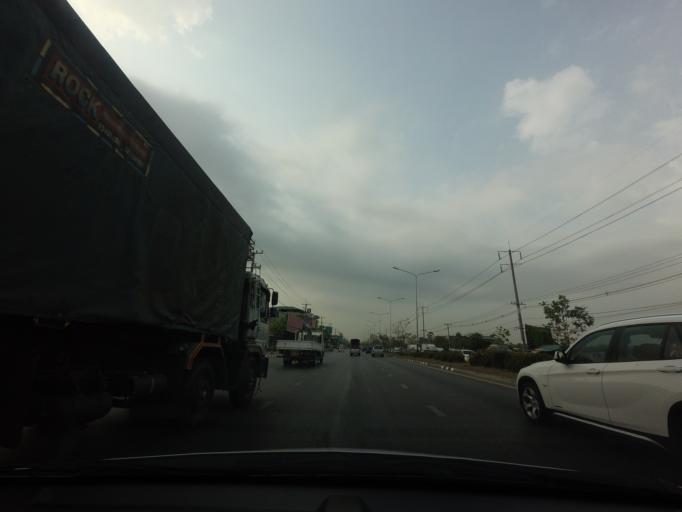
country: TH
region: Bangkok
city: Thawi Watthana
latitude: 13.7663
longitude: 100.3285
